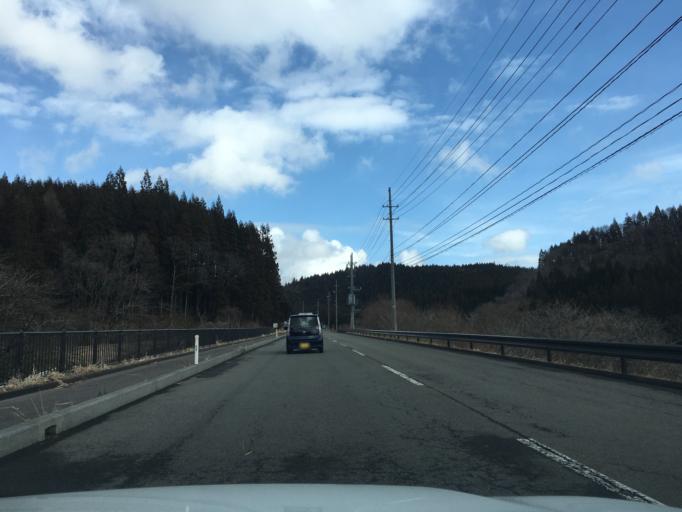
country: JP
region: Akita
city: Takanosu
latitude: 40.0910
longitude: 140.3373
